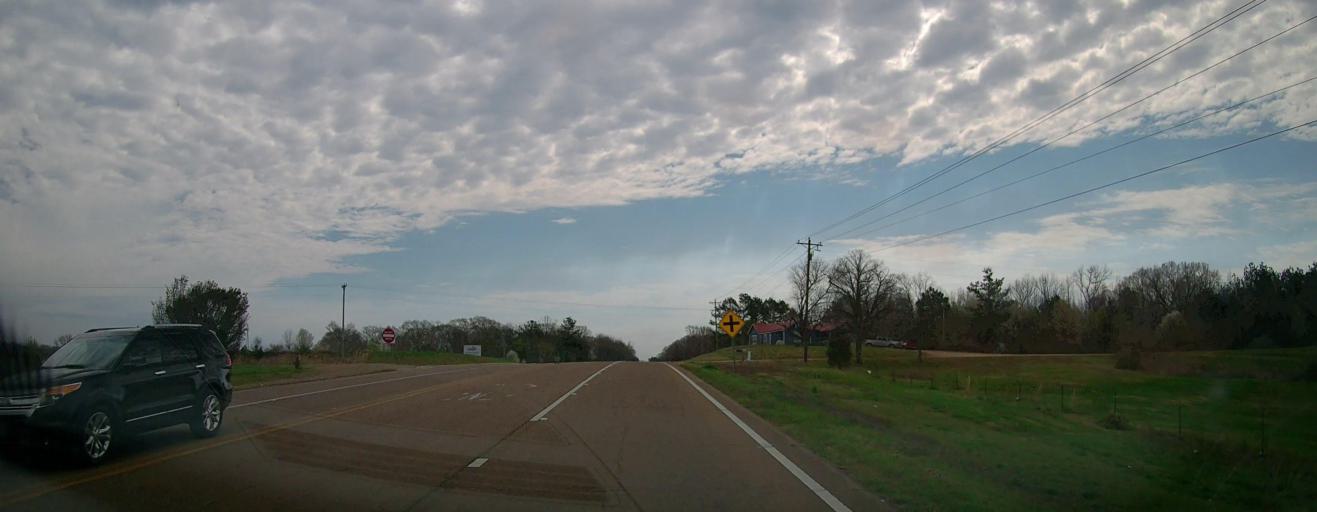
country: US
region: Mississippi
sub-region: Marshall County
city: Byhalia
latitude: 34.8618
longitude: -89.6563
